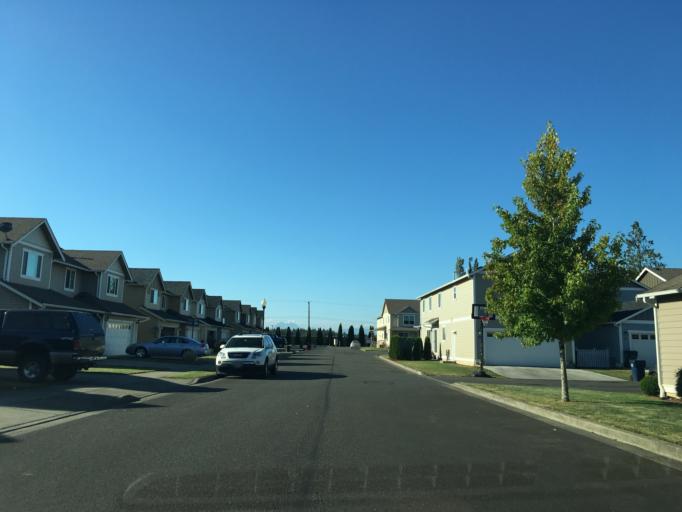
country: US
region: Washington
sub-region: Whatcom County
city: Lynden
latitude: 48.9633
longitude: -122.4599
